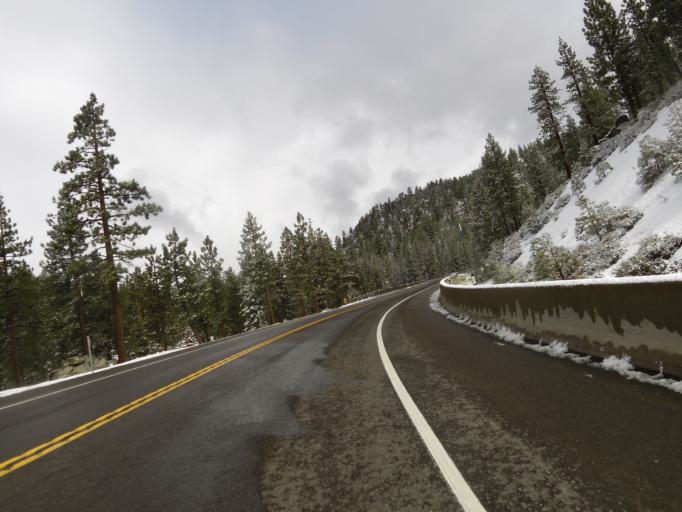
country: US
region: Nevada
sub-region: Douglas County
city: Kingsbury
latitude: 38.9767
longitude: -119.8841
